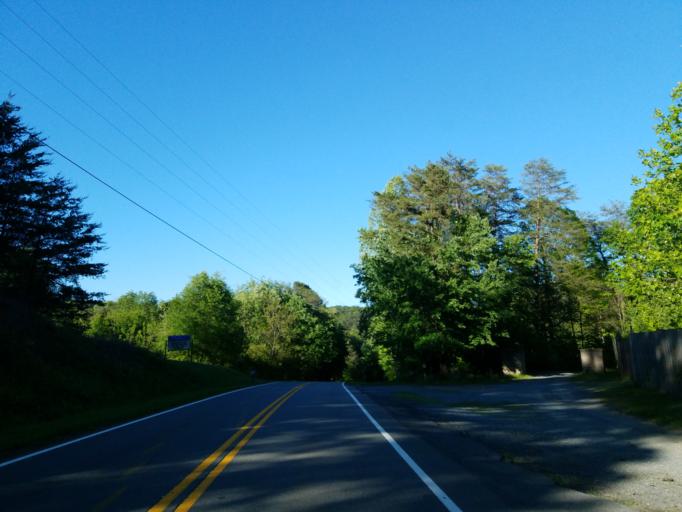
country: US
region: Georgia
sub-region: Gilmer County
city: Ellijay
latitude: 34.6736
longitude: -84.3443
